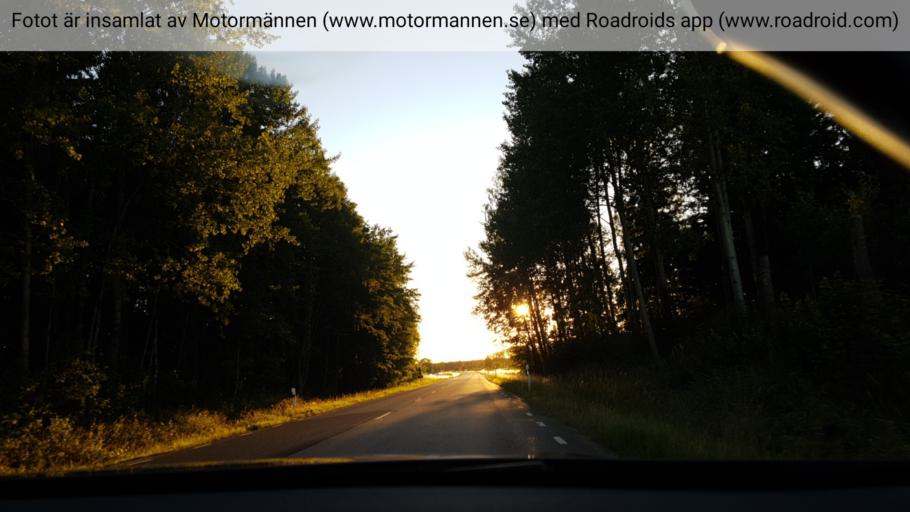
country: SE
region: Vaestra Goetaland
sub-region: Tidaholms Kommun
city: Olofstorp
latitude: 58.3686
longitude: 14.0117
